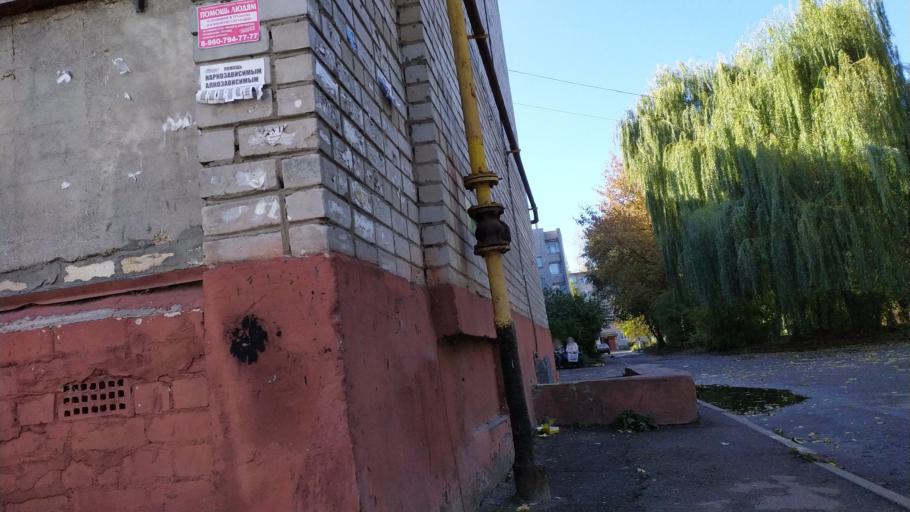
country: RU
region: Kursk
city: Kursk
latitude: 51.6508
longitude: 36.1420
